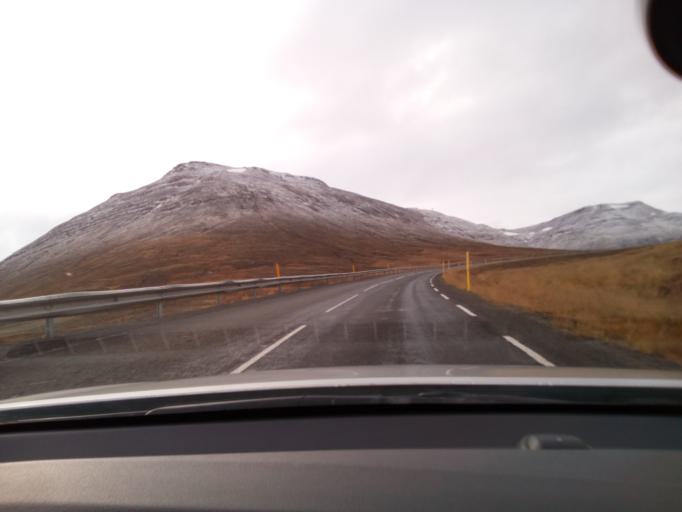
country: IS
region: Northeast
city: Dalvik
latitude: 65.4734
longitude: -18.6705
